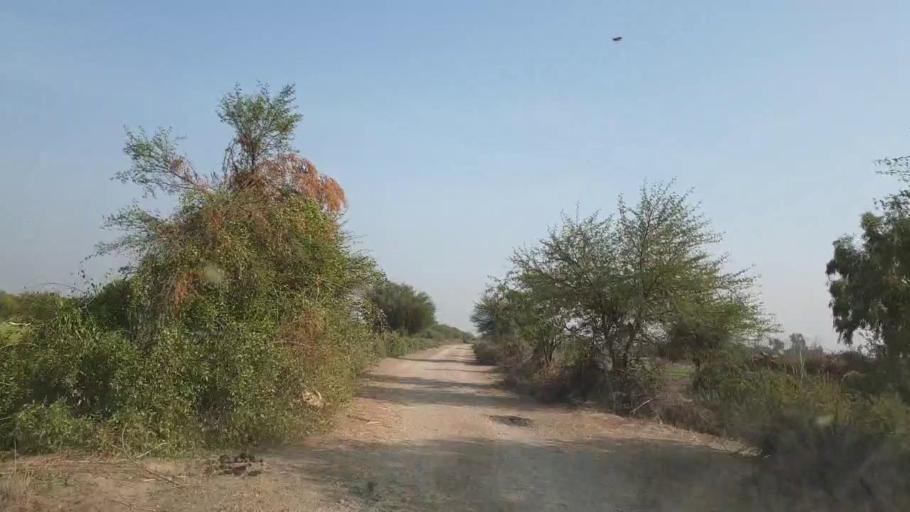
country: PK
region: Sindh
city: Pithoro
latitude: 25.6771
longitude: 69.2362
